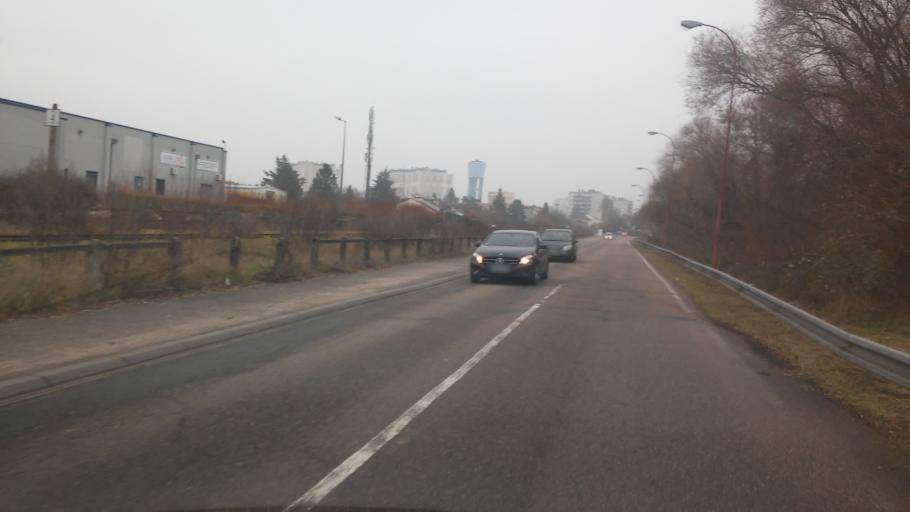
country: FR
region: Lorraine
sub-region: Departement de la Moselle
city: Montigny-les-Metz
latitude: 49.0809
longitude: 6.1501
